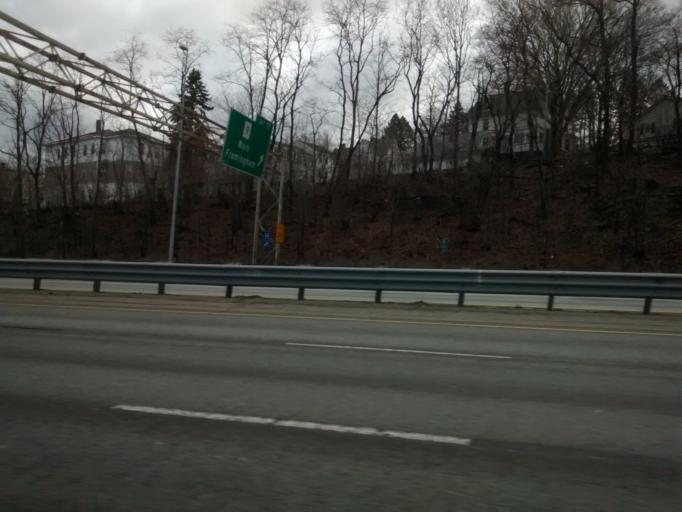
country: US
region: Massachusetts
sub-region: Worcester County
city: Worcester
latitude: 42.2697
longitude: -71.7938
